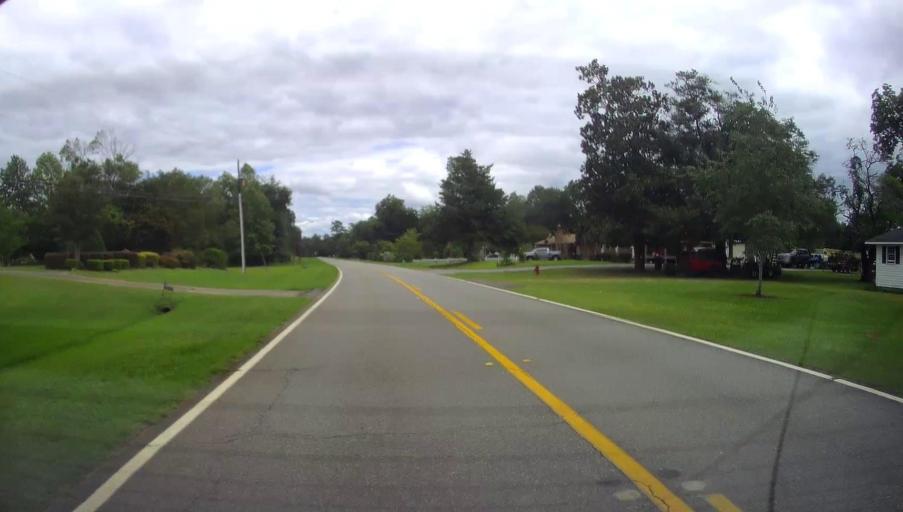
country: US
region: Georgia
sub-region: Twiggs County
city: Jeffersonville
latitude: 32.6807
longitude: -83.3336
